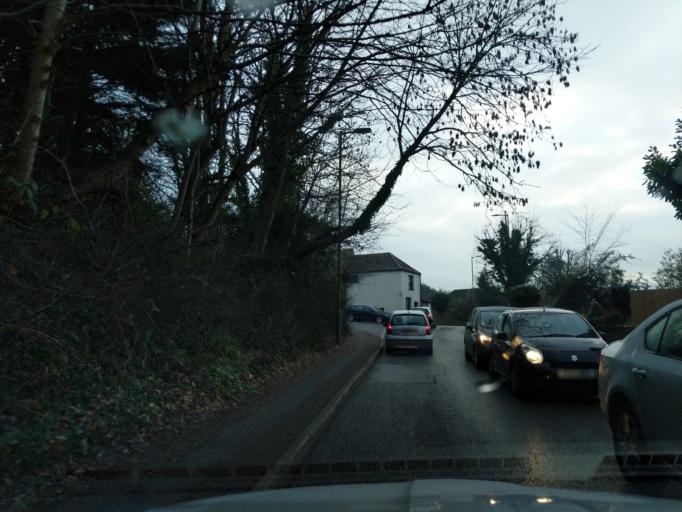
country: GB
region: England
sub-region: Hertfordshire
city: Abbots Langley
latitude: 51.7015
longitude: -0.4349
